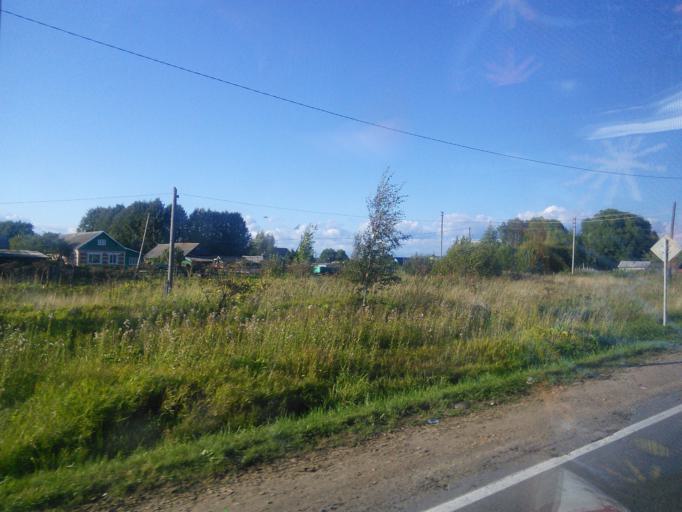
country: RU
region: Jaroslavl
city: Poshekhon'ye
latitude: 58.4237
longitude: 38.9921
